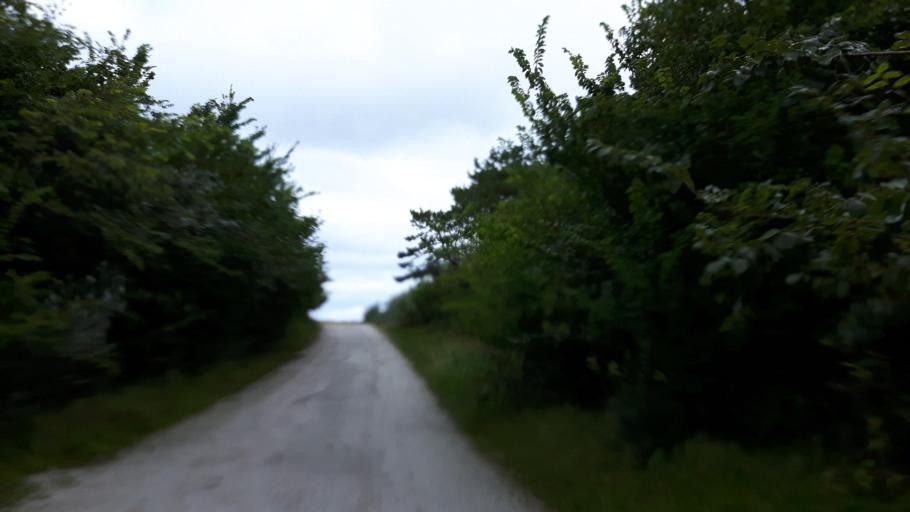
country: NL
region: Friesland
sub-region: Gemeente Ameland
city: Nes
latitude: 53.4555
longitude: 5.7578
